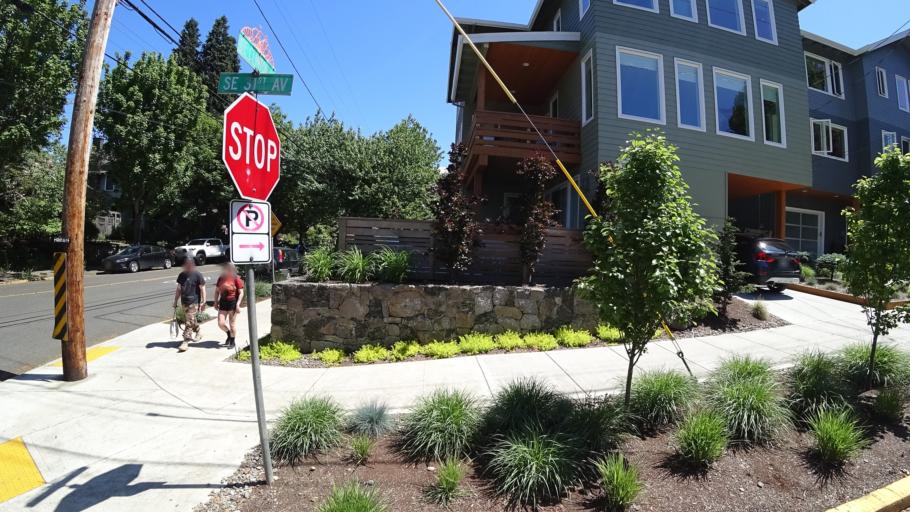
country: US
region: Oregon
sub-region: Multnomah County
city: Portland
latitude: 45.5034
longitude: -122.6336
